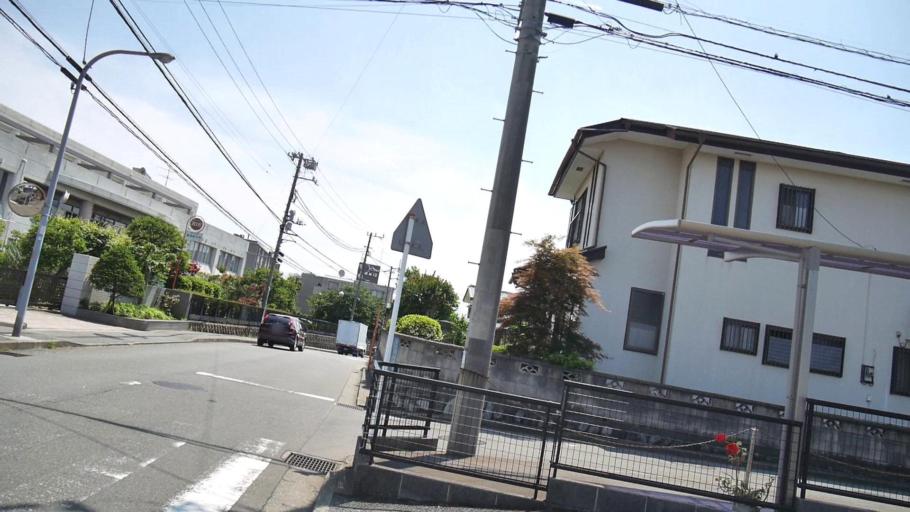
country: JP
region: Kanagawa
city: Fujisawa
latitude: 35.4000
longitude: 139.5159
